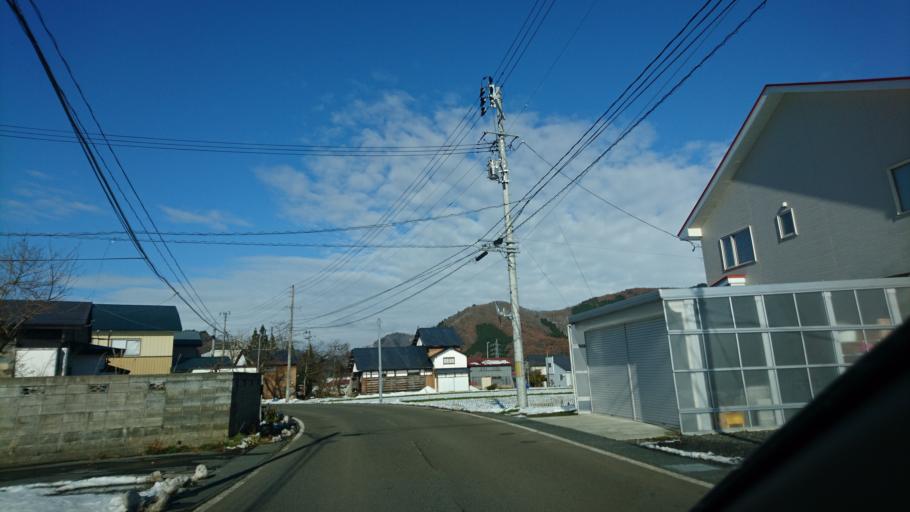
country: JP
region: Akita
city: Yokotemachi
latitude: 39.3089
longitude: 140.7781
